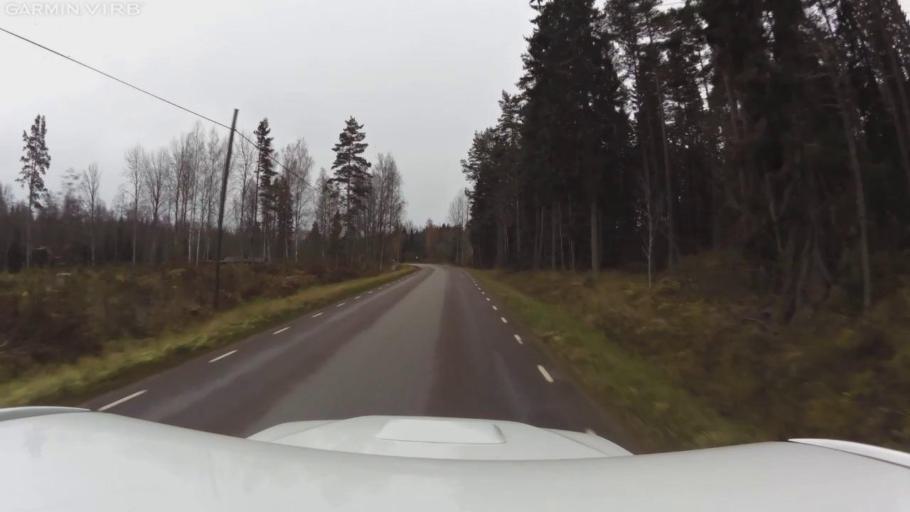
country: SE
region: OEstergoetland
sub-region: Linkopings Kommun
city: Vikingstad
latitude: 58.2475
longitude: 15.3866
